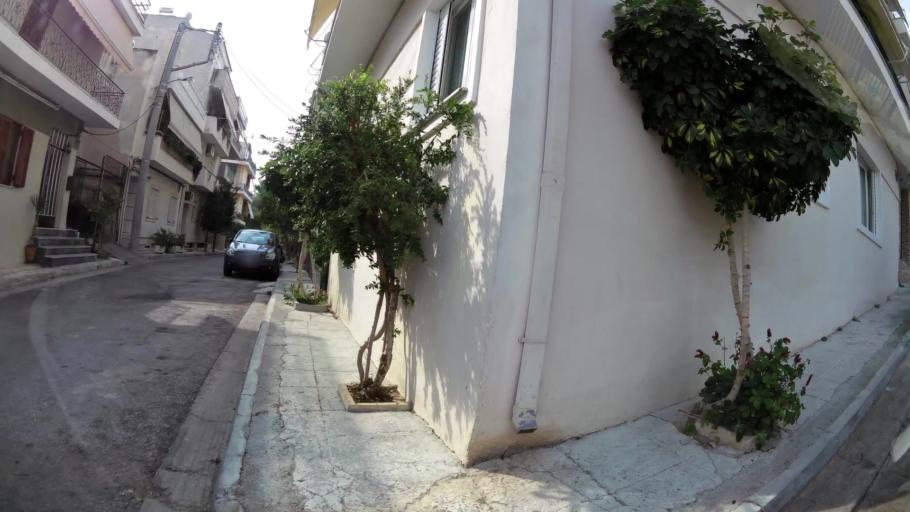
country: GR
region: Attica
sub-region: Nomarchia Athinas
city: Chaidari
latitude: 38.0165
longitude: 23.6745
